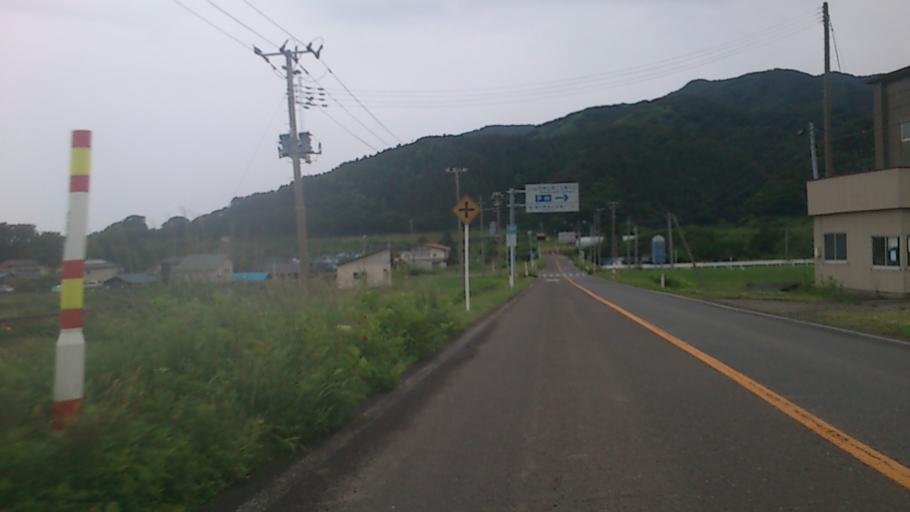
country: JP
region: Akita
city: Noshiromachi
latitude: 40.3748
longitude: 140.0161
